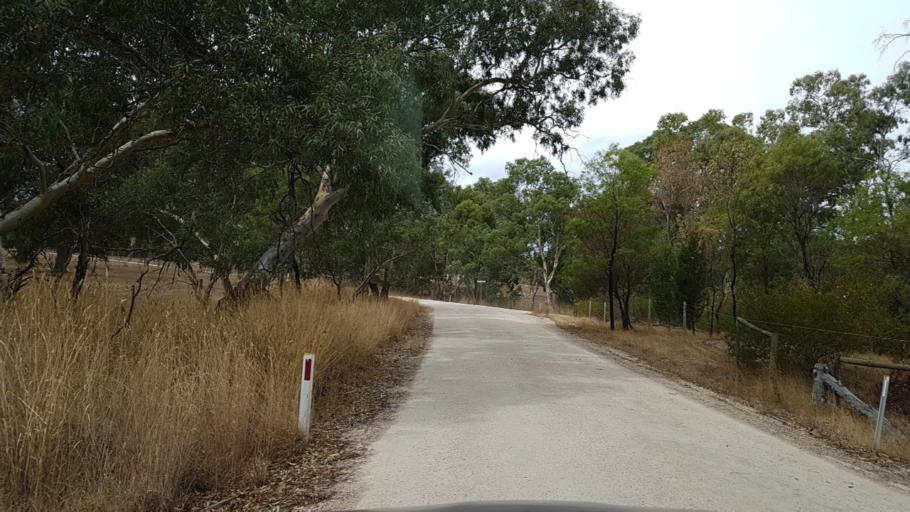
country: AU
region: South Australia
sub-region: Adelaide Hills
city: Birdwood
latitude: -34.7843
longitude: 138.9869
